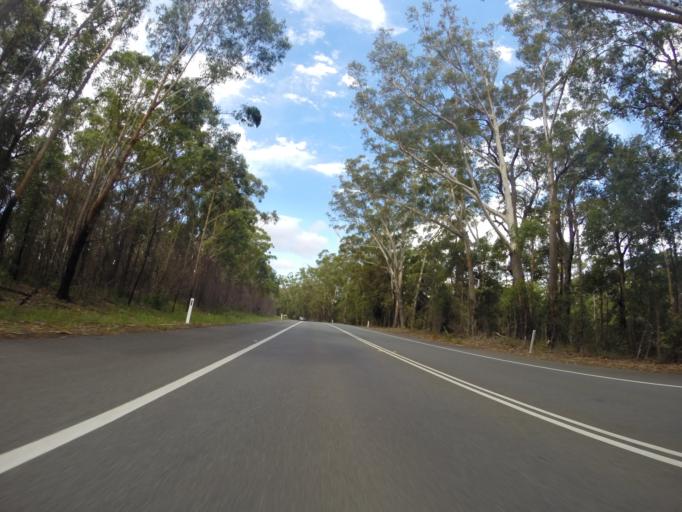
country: AU
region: New South Wales
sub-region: Shoalhaven Shire
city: Milton
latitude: -35.1510
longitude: 150.4567
